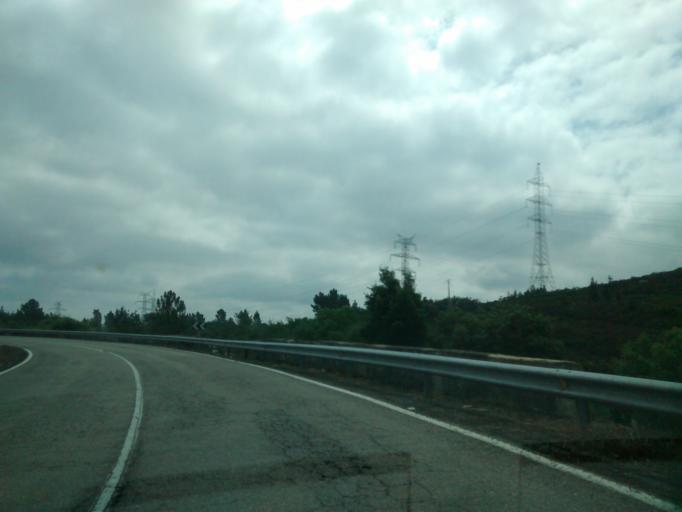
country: ES
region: Galicia
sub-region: Provincia de Ourense
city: Manzaneda
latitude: 42.3366
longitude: -7.1838
